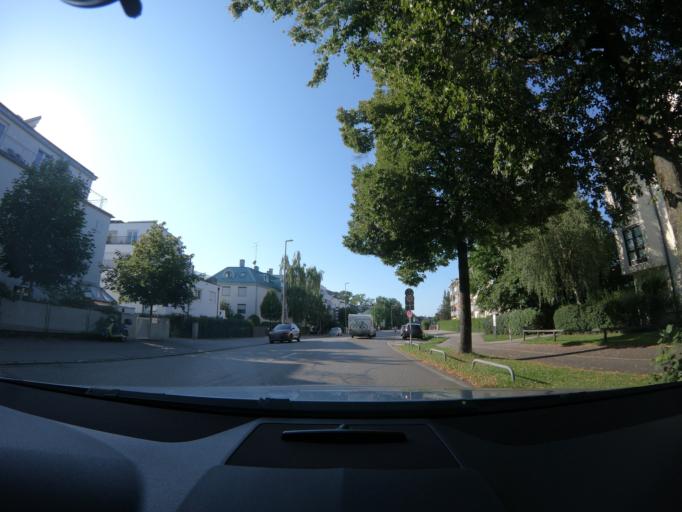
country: DE
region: Bavaria
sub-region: Upper Bavaria
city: Unterhaching
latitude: 48.1079
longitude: 11.6193
